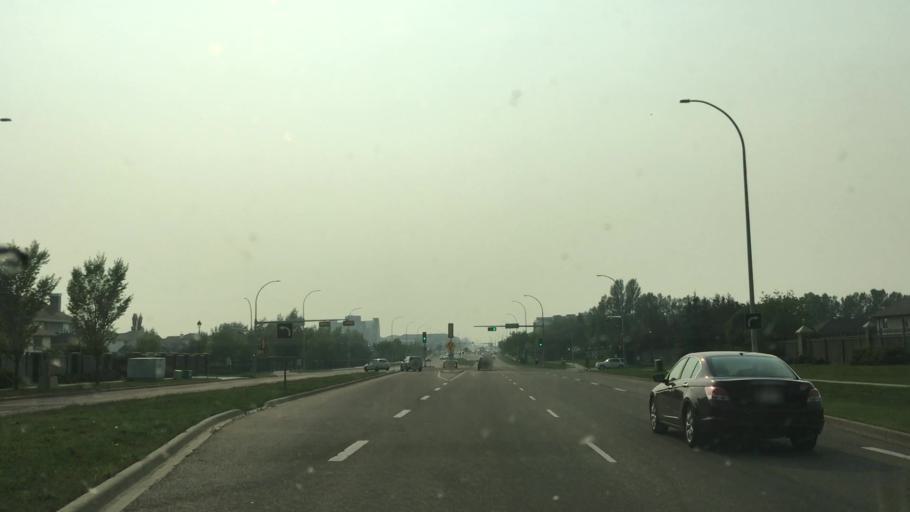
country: CA
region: Alberta
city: Beaumont
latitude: 53.4249
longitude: -113.5073
